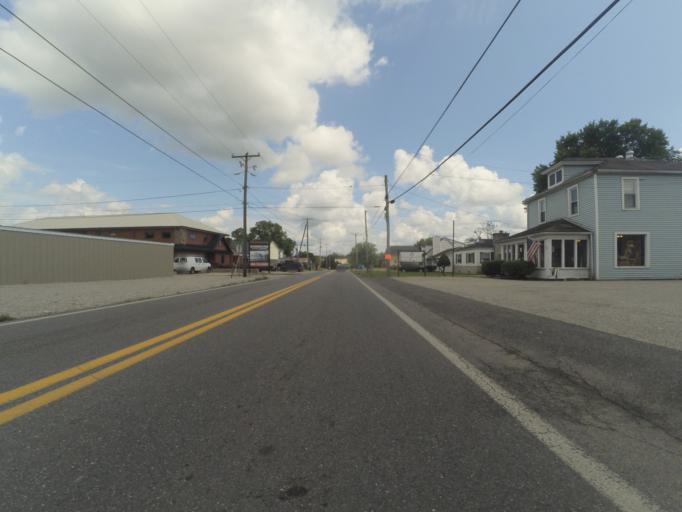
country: US
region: West Virginia
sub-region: Cabell County
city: Barboursville
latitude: 38.4176
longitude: -82.3040
